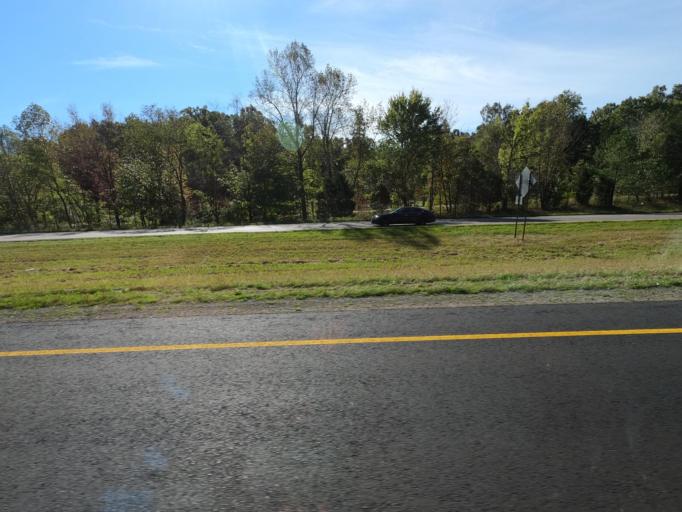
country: US
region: Tennessee
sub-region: Dickson County
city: Burns
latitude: 36.0225
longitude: -87.3190
